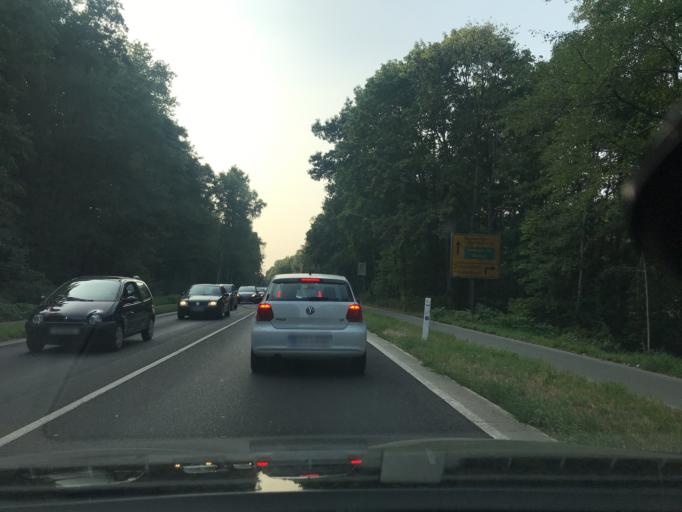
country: DE
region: North Rhine-Westphalia
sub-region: Regierungsbezirk Dusseldorf
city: Erkrath
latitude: 51.2096
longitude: 6.8761
